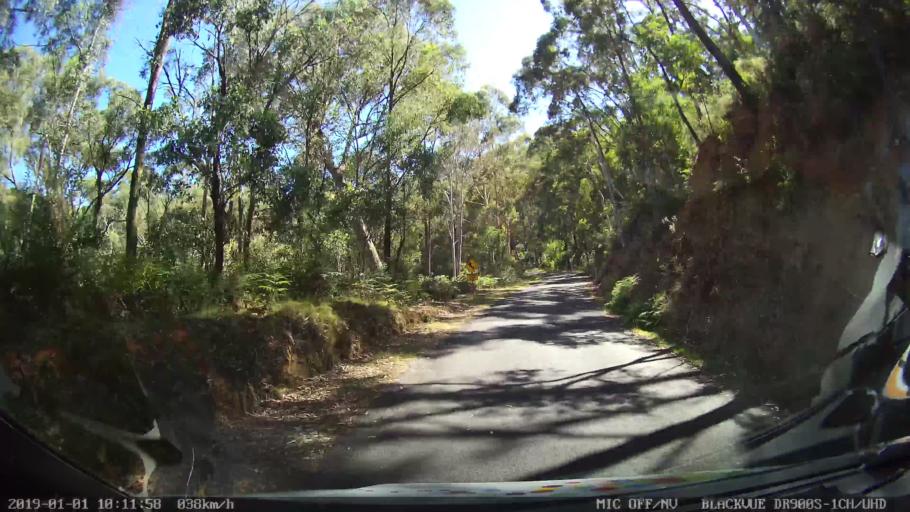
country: AU
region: New South Wales
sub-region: Snowy River
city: Jindabyne
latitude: -36.1342
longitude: 148.1565
